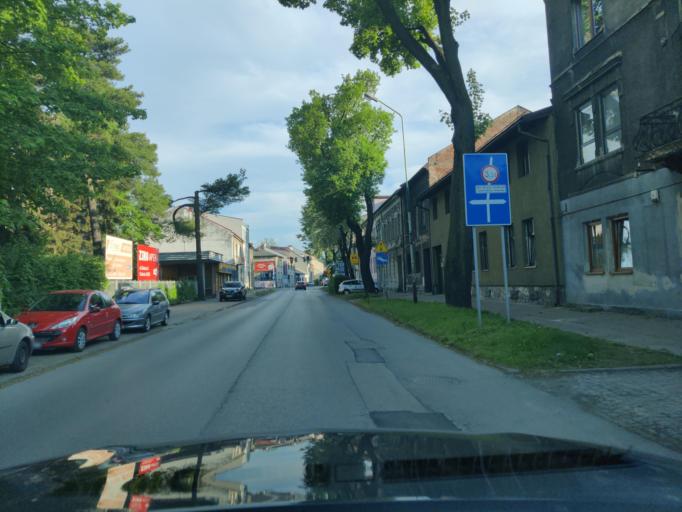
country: PL
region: Silesian Voivodeship
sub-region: Powiat zywiecki
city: Zywiec
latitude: 49.6931
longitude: 19.2030
